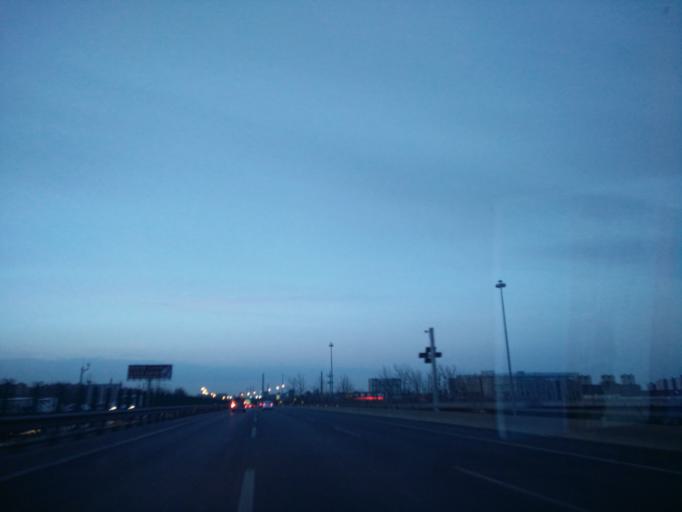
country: CN
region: Beijing
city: Dongfeng
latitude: 39.8681
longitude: 116.5425
